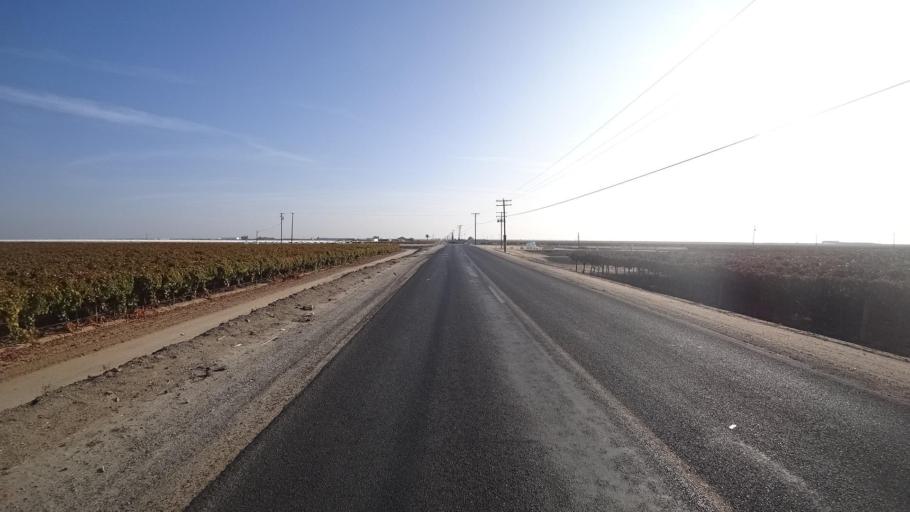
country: US
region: California
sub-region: Kern County
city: McFarland
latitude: 35.6746
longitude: -119.1972
